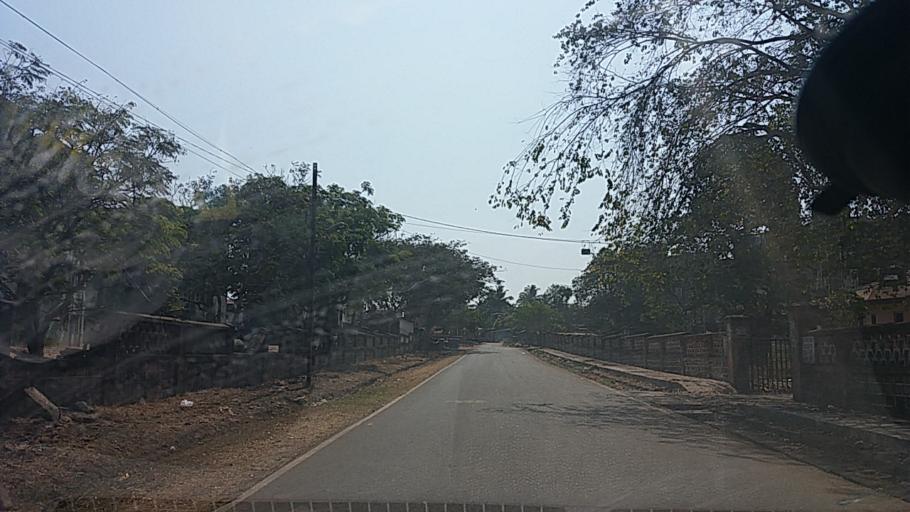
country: IN
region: Goa
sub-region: South Goa
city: Marmagao
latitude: 15.4080
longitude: 73.7901
